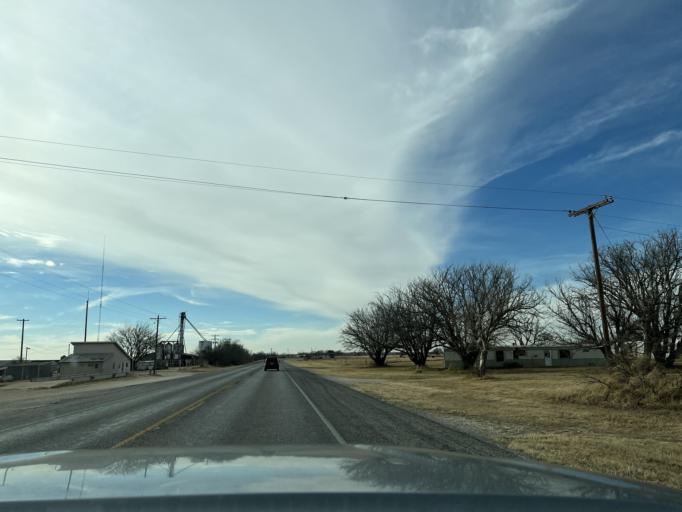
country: US
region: Texas
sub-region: Fisher County
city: Roby
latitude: 32.7543
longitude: -100.2580
